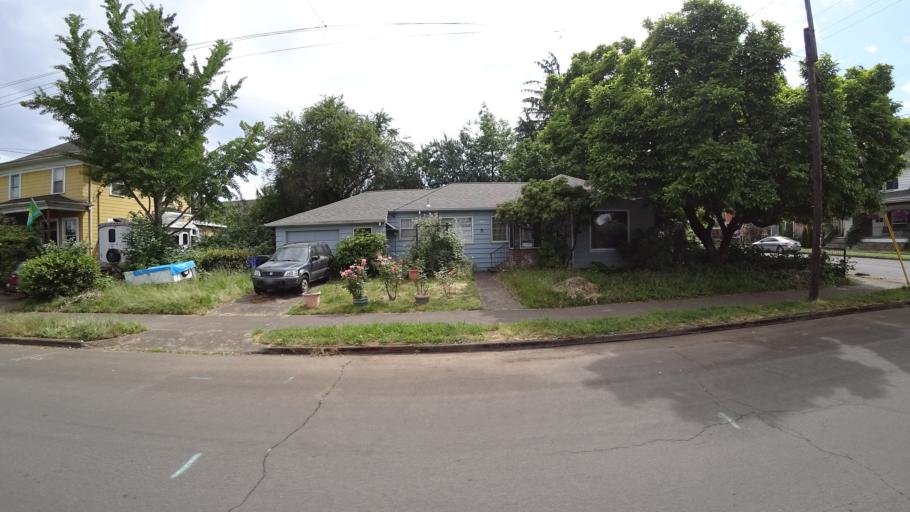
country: US
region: Oregon
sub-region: Washington County
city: West Haven
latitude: 45.5880
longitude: -122.7484
